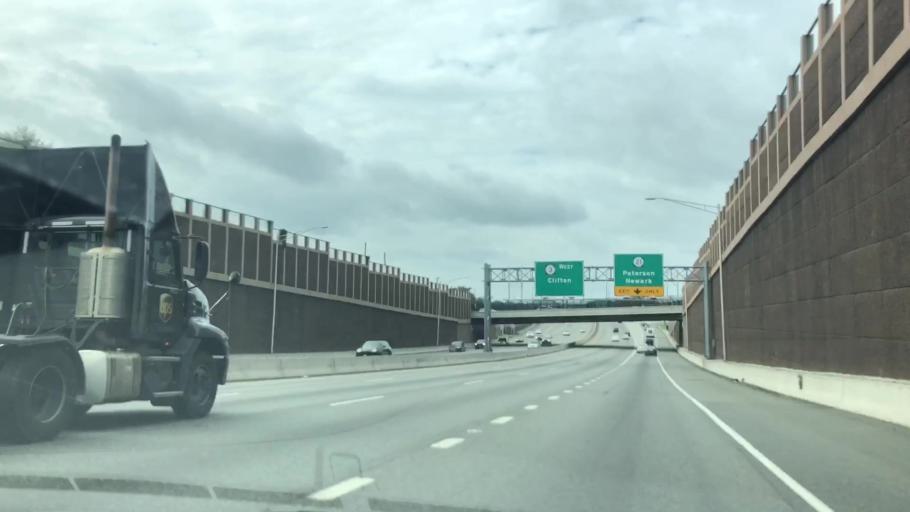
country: US
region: New Jersey
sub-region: Bergen County
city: Lyndhurst
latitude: 40.8201
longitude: -74.1190
